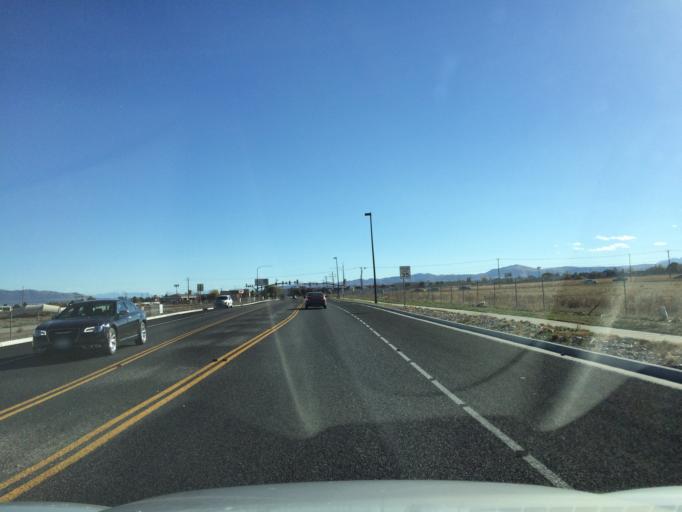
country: US
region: Utah
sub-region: Salt Lake County
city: Oquirrh
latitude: 40.6115
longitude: -111.9976
